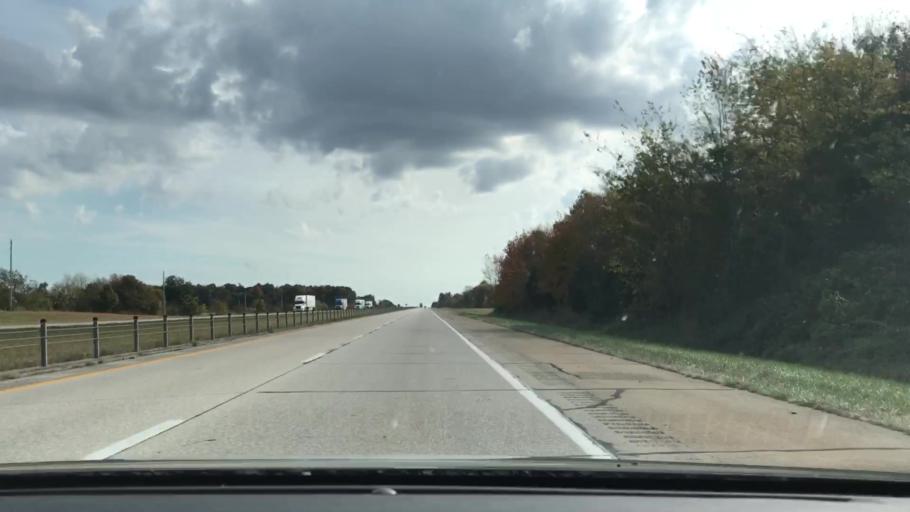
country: US
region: Kentucky
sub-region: Caldwell County
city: Princeton
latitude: 36.9970
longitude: -87.9390
